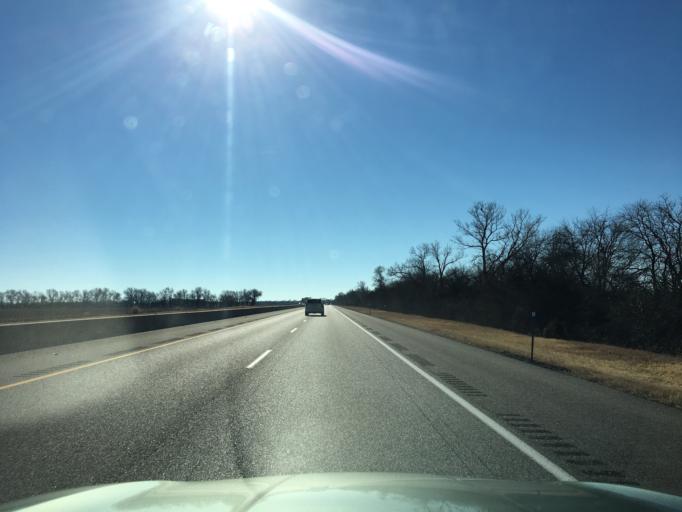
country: US
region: Kansas
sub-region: Sumner County
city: Belle Plaine
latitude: 37.4328
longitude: -97.3214
